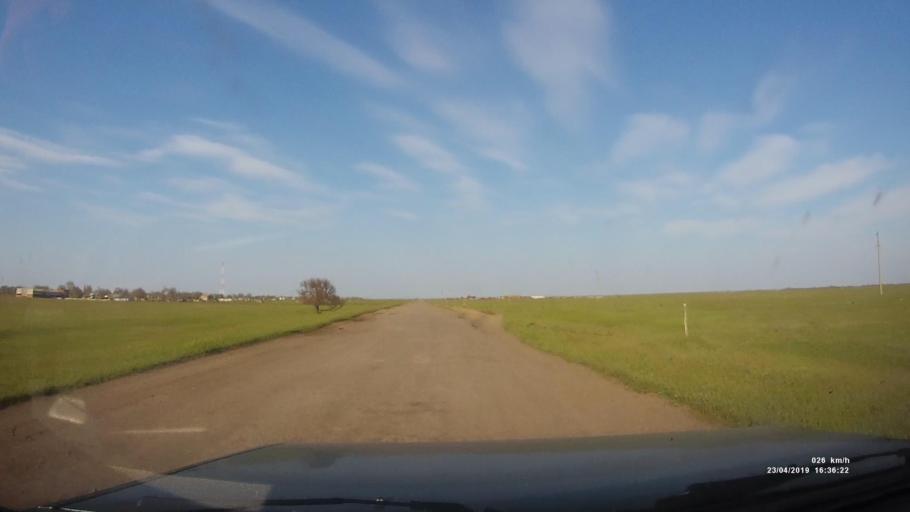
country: RU
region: Kalmykiya
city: Priyutnoye
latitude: 46.3295
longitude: 43.1405
